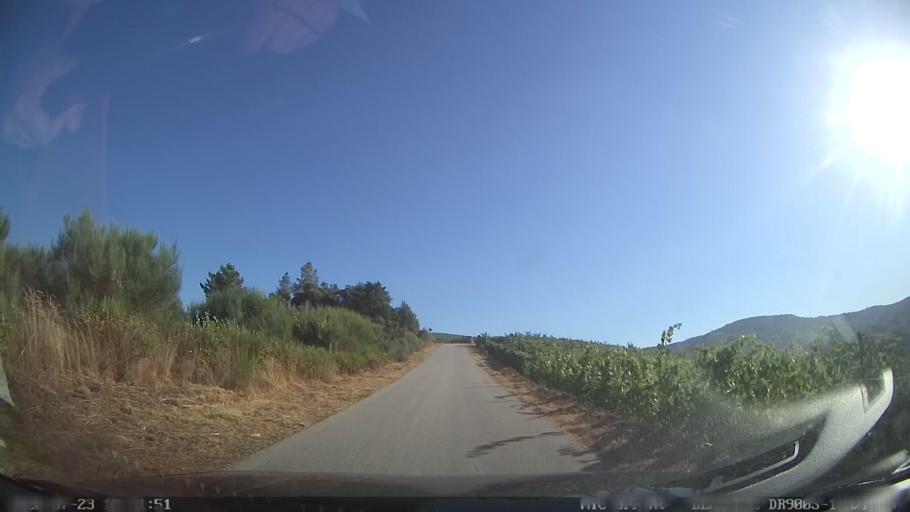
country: PT
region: Viseu
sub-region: Sao Joao da Pesqueira
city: Sao Joao da Pesqueira
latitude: 41.1752
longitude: -7.4066
